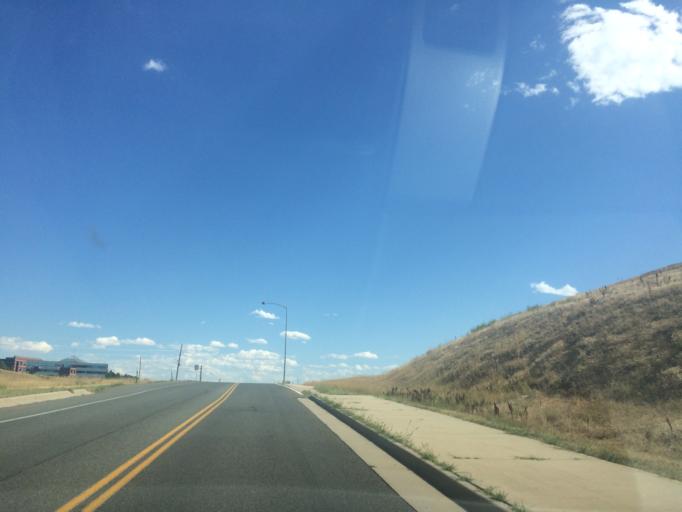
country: US
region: Colorado
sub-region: Broomfield County
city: Broomfield
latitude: 39.9297
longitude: -105.1157
